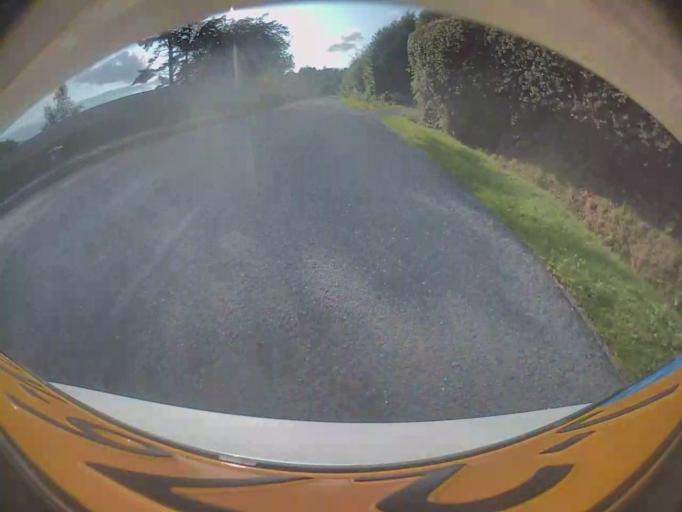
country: IE
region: Leinster
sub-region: Wicklow
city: Enniskerry
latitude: 53.1887
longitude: -6.2339
